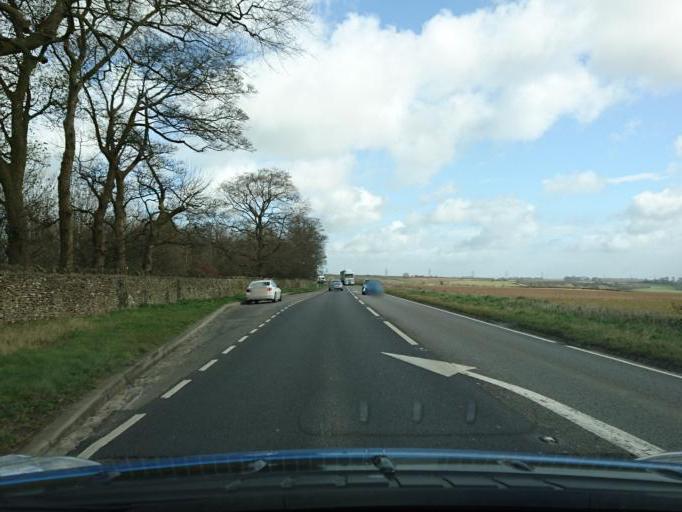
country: GB
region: England
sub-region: South Gloucestershire
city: Cold Ashton
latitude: 51.4755
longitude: -2.3635
